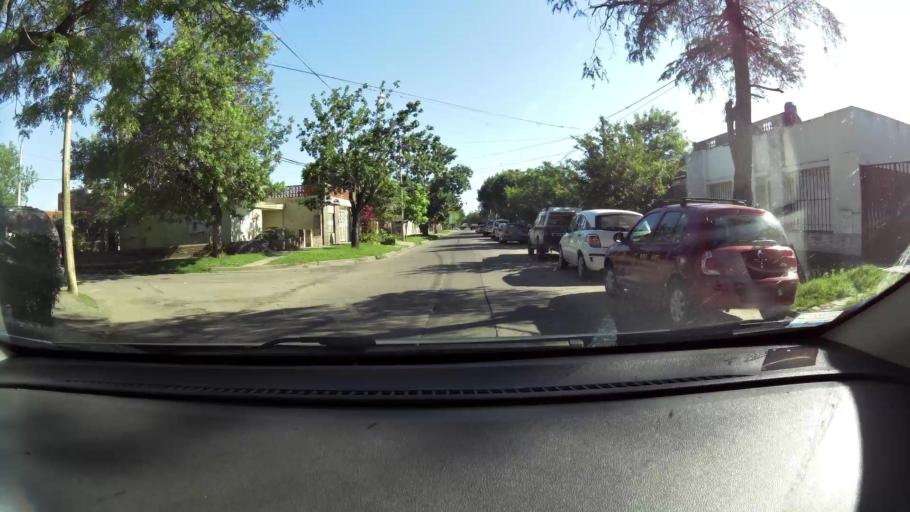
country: AR
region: Santa Fe
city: Santa Fe de la Vera Cruz
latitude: -31.6084
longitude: -60.6801
